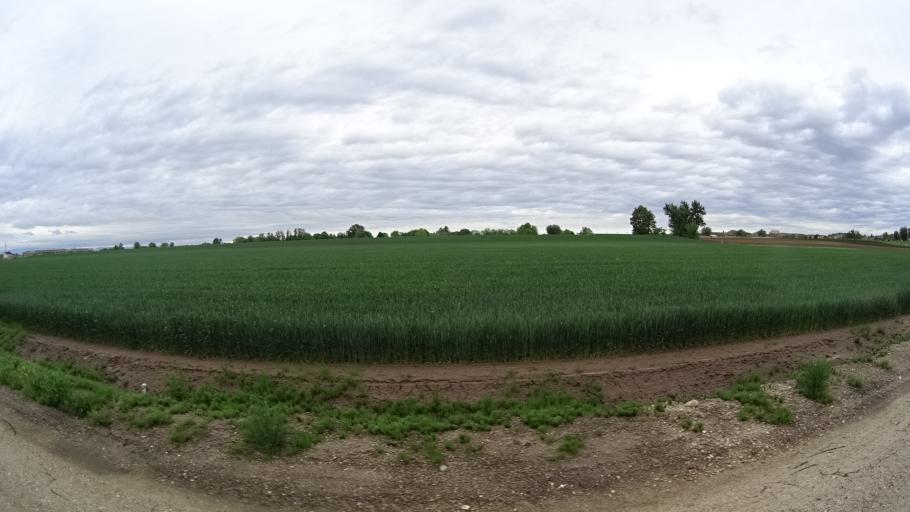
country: US
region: Idaho
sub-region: Ada County
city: Star
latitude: 43.7165
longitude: -116.4680
